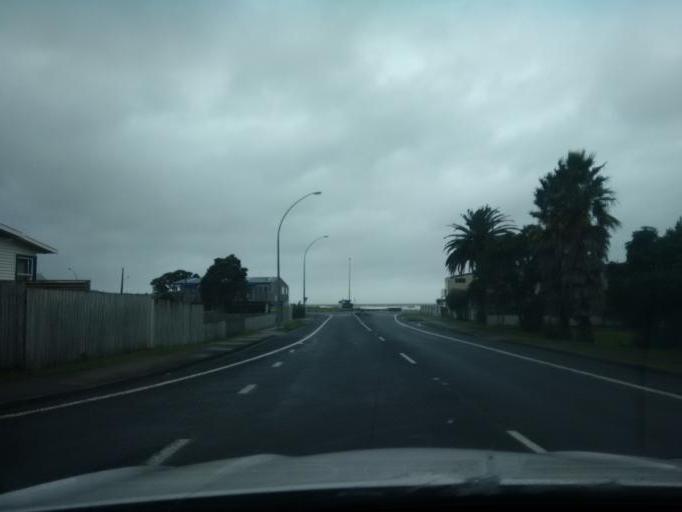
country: NZ
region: Waikato
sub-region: Thames-Coromandel District
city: Whitianga
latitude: -36.8198
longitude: 175.6984
